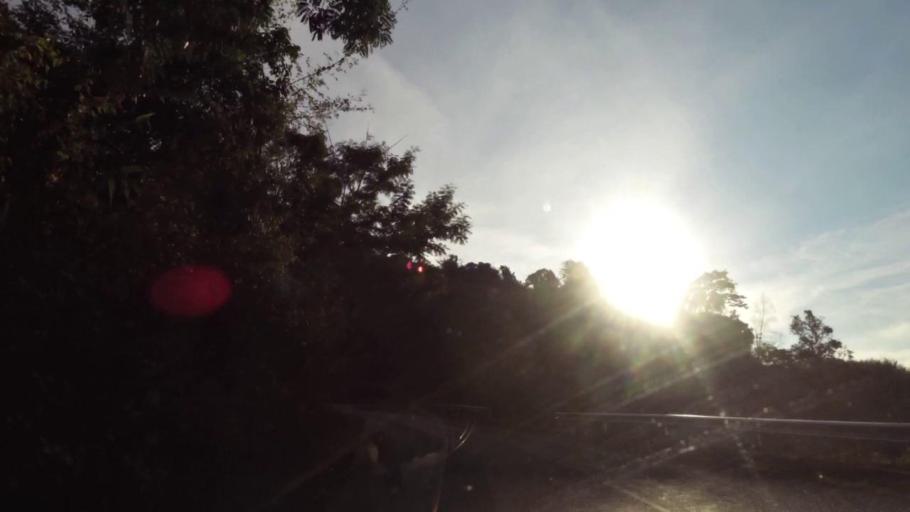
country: TH
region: Chiang Rai
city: Khun Tan
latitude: 19.8616
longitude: 100.4382
